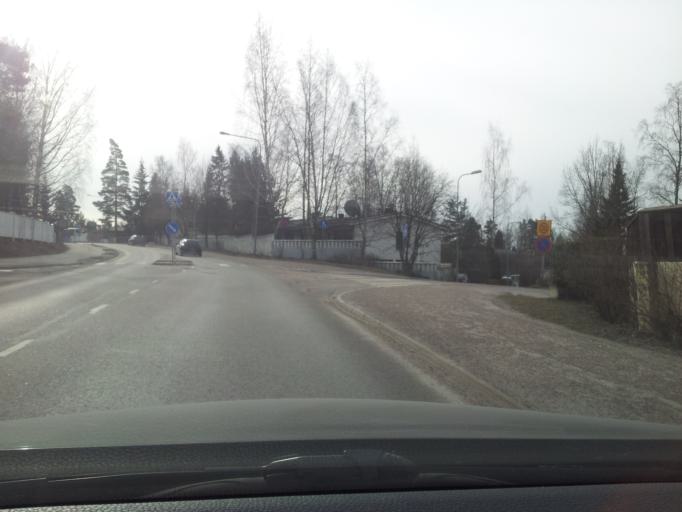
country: FI
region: Uusimaa
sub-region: Helsinki
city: Kilo
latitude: 60.1883
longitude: 24.7821
